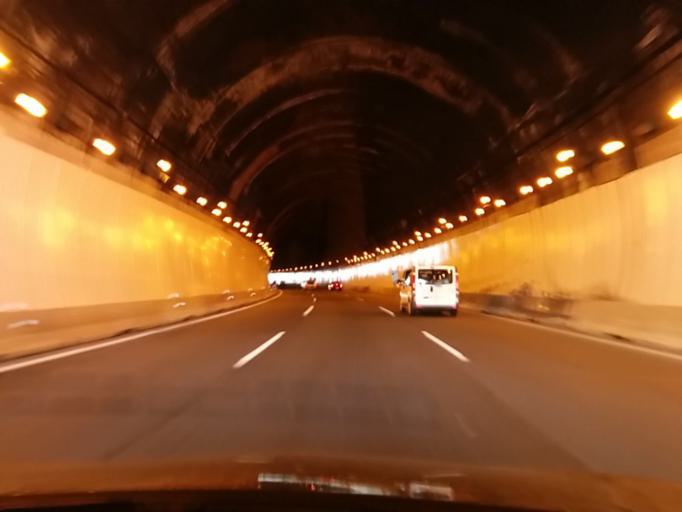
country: ES
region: Basque Country
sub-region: Provincia de Guipuzcoa
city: San Sebastian
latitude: 43.3163
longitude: -1.9628
